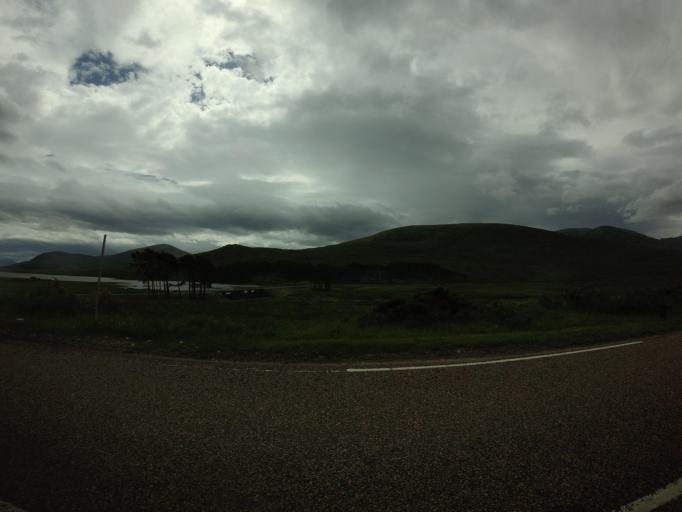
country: GB
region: Scotland
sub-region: Highland
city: Ullapool
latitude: 57.7355
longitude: -4.9367
